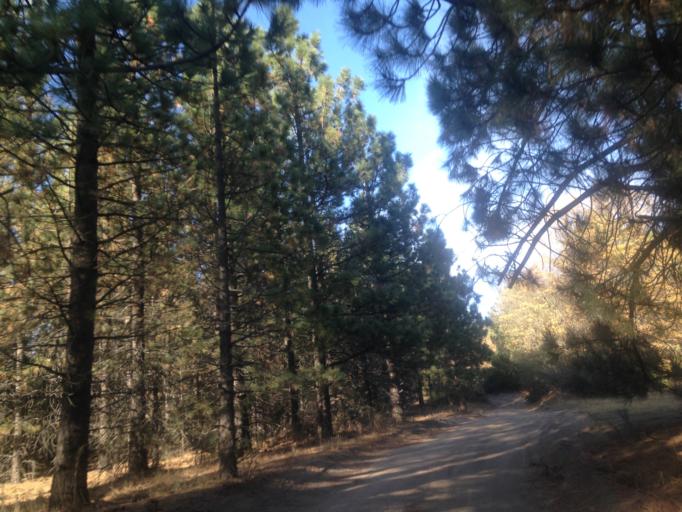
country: US
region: California
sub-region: San Bernardino County
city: Yucaipa
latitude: 34.1323
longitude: -117.0121
